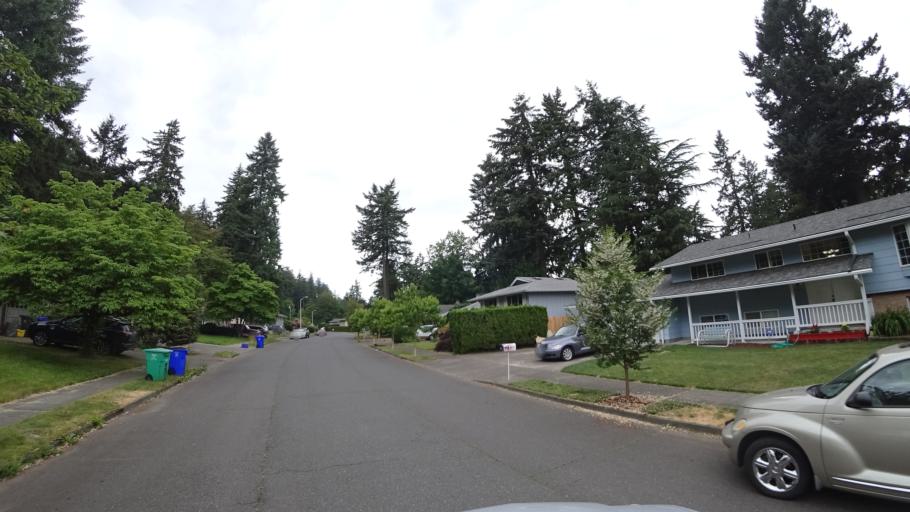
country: US
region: Oregon
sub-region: Clackamas County
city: Happy Valley
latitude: 45.4939
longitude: -122.5058
